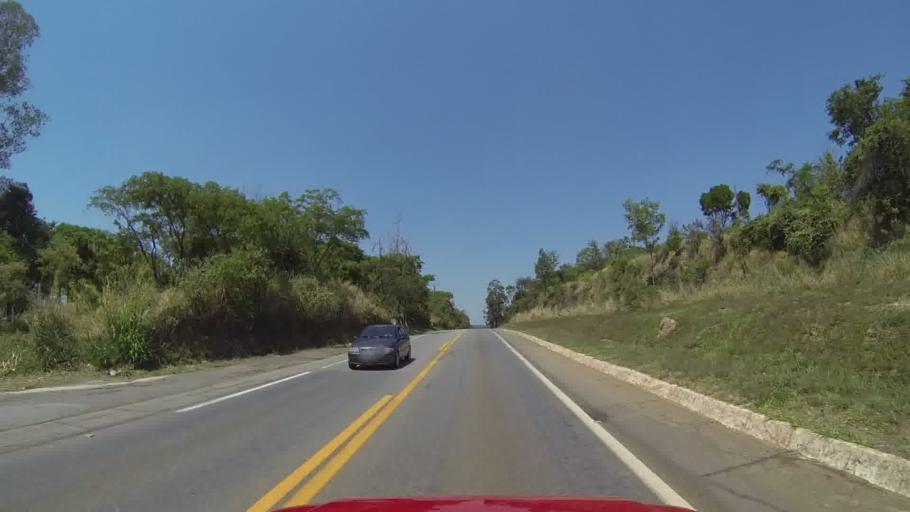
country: BR
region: Minas Gerais
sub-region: Itauna
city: Itauna
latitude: -20.0525
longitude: -44.5430
